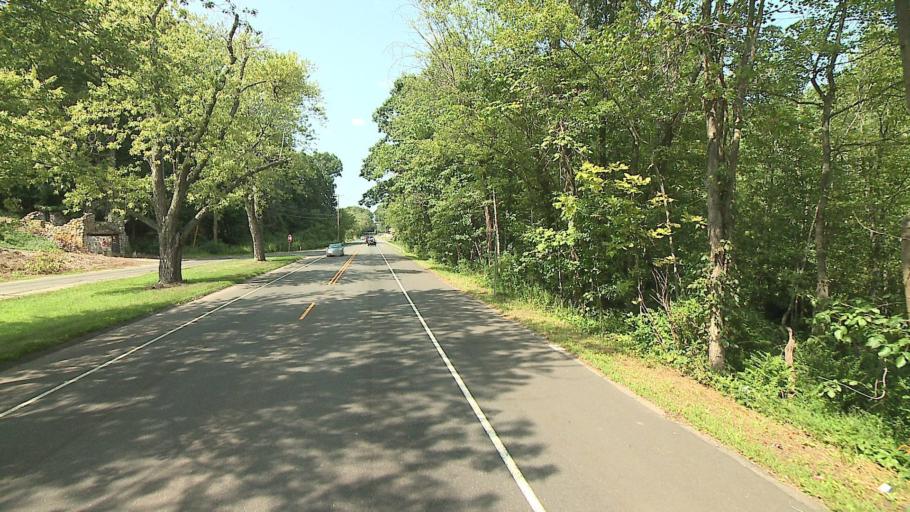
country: US
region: Connecticut
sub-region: Fairfield County
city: Trumbull
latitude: 41.3082
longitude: -73.2566
